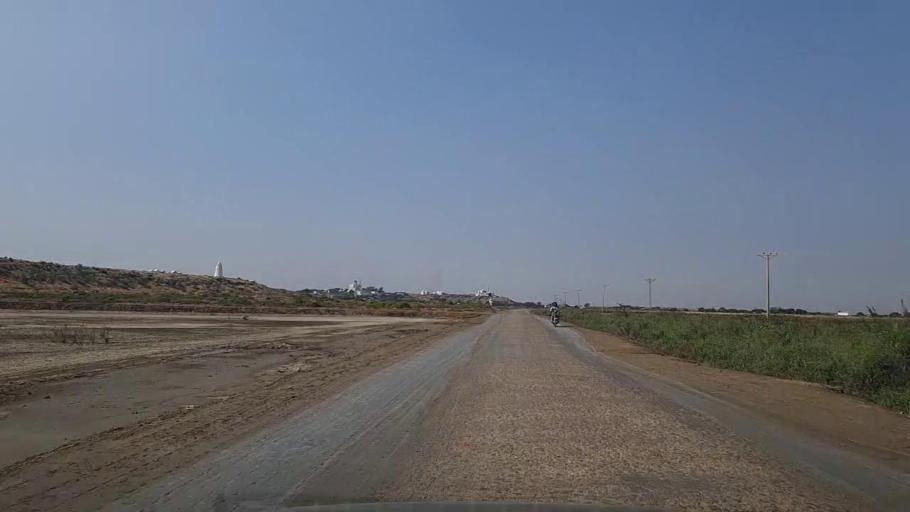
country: PK
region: Sindh
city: Chuhar Jamali
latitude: 24.5534
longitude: 67.8905
